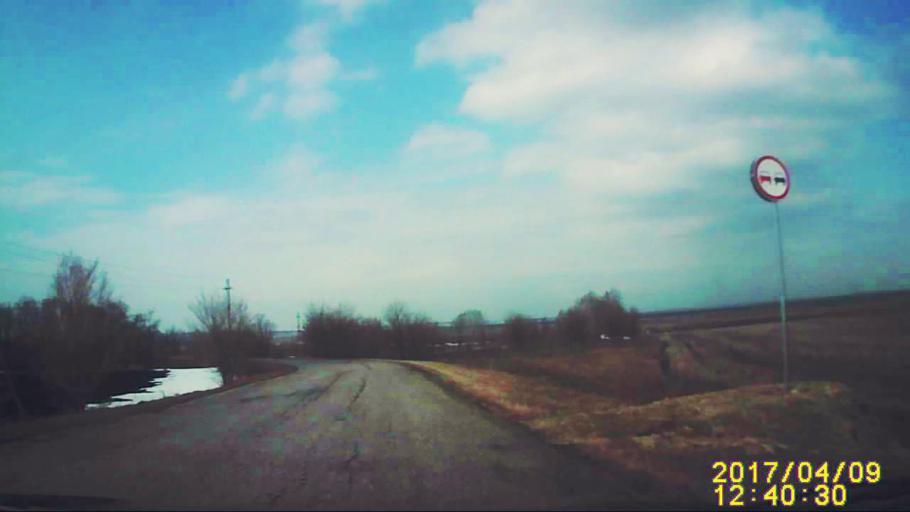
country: RU
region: Ulyanovsk
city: Ignatovka
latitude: 54.0032
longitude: 47.9458
